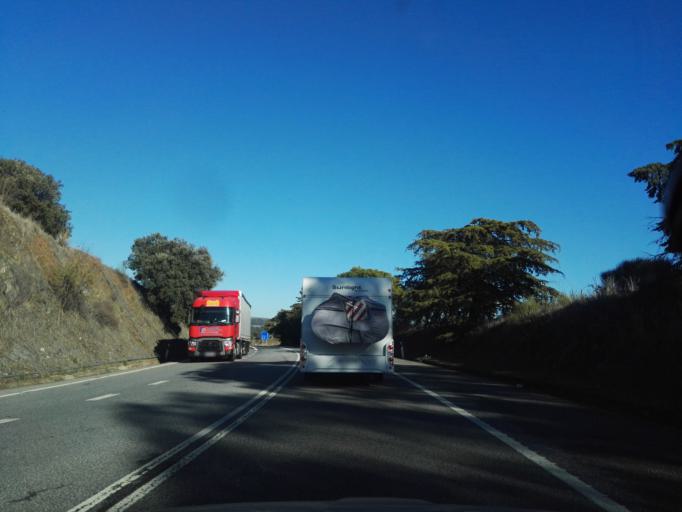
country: PT
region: Evora
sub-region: Vila Vicosa
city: Vila Vicosa
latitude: 38.8491
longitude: -7.3382
